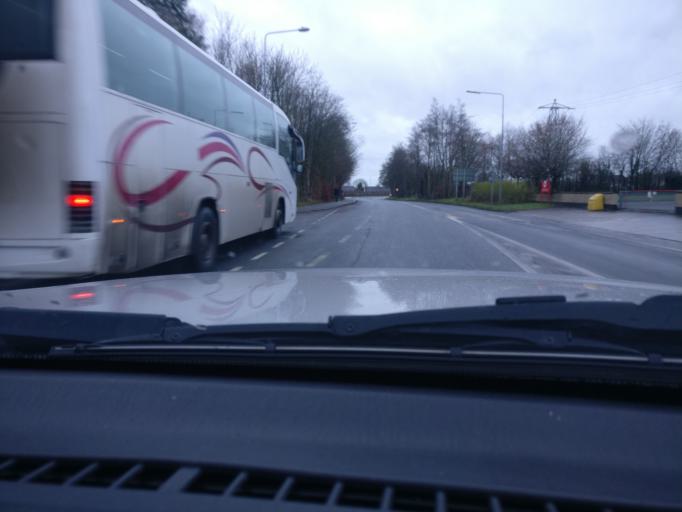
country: IE
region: Leinster
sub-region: An Mhi
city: Trim
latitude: 53.5513
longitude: -6.7871
